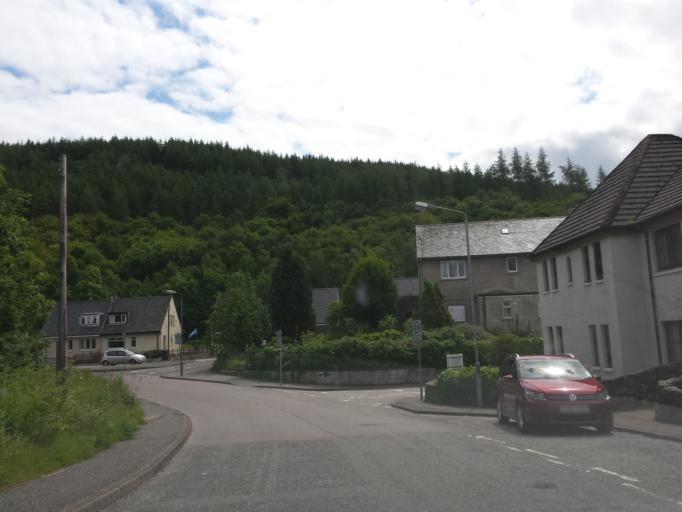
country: GB
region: Scotland
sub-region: Argyll and Bute
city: Oban
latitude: 56.4453
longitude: -5.4420
